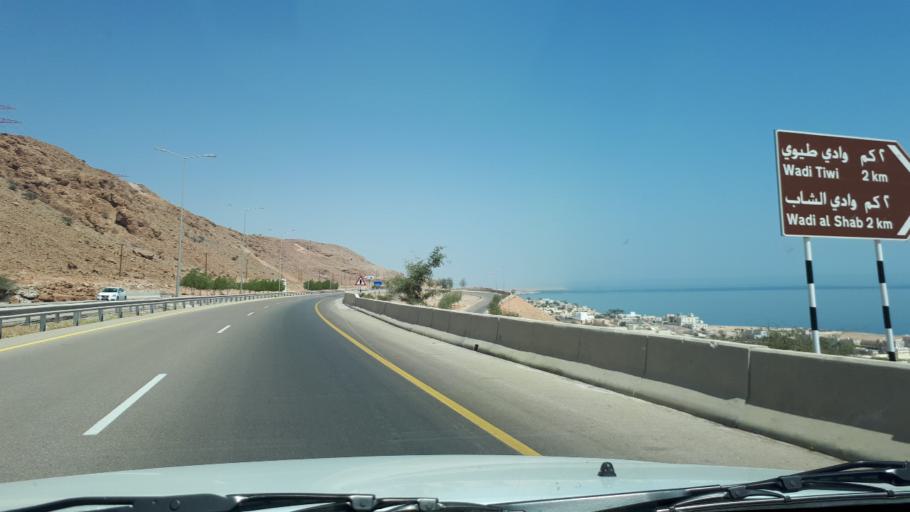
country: OM
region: Ash Sharqiyah
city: Sur
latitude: 22.8265
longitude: 59.2537
